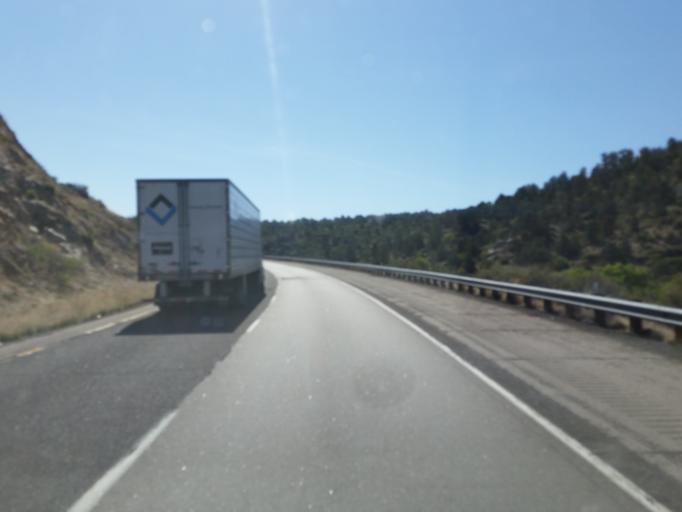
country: US
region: Arizona
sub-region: Mohave County
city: Peach Springs
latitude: 35.1766
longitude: -113.4793
